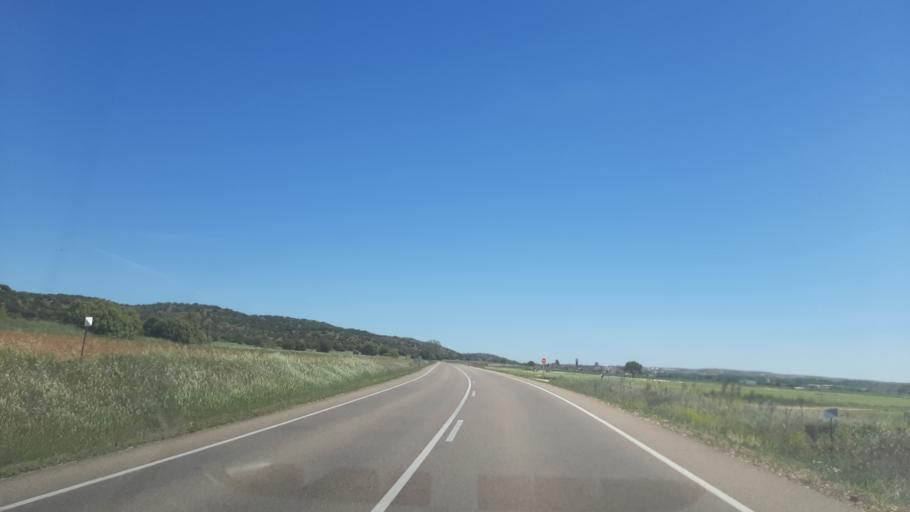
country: ES
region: Castille and Leon
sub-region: Provincia de Salamanca
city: Encinas de Arriba
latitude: 40.7879
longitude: -5.5502
